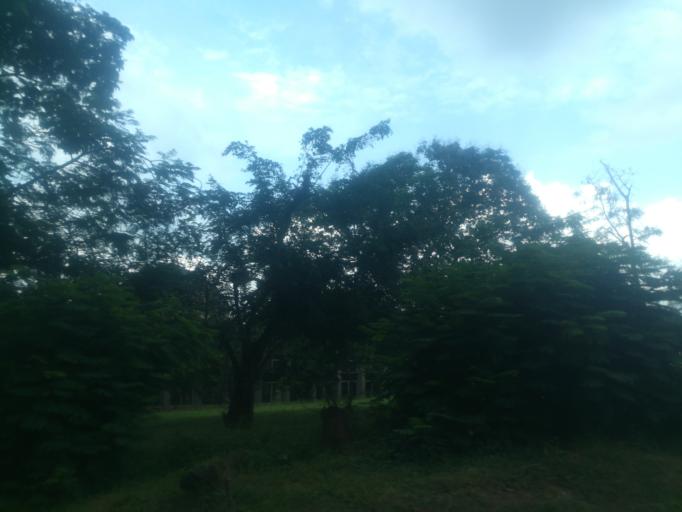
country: NG
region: Oyo
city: Ibadan
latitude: 7.4465
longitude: 3.8995
